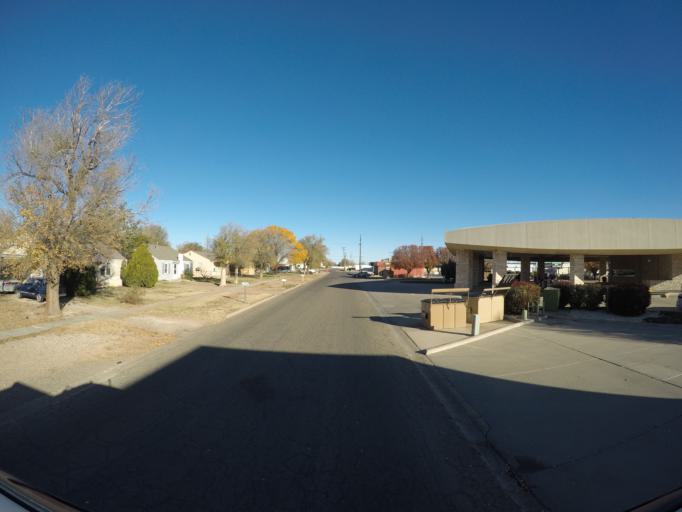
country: US
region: New Mexico
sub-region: Curry County
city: Clovis
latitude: 34.4181
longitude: -103.1978
